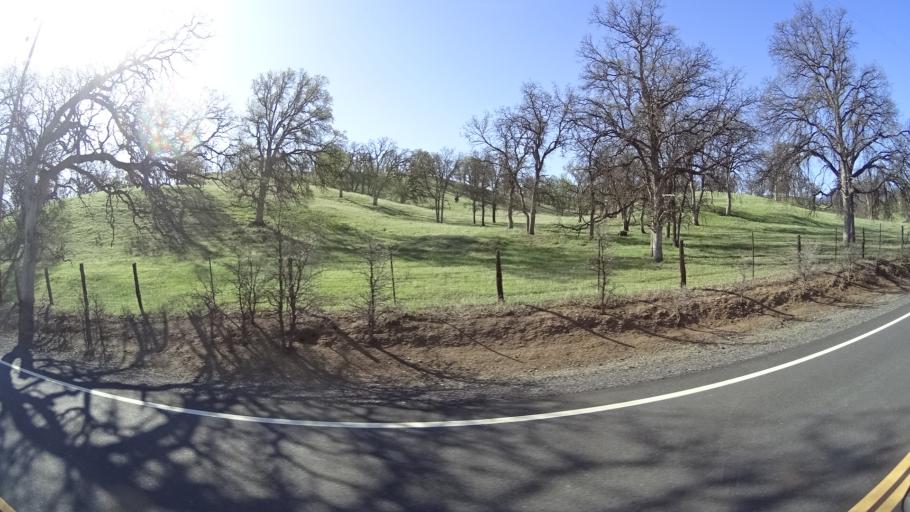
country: US
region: California
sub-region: Glenn County
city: Orland
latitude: 39.6604
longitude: -122.5337
